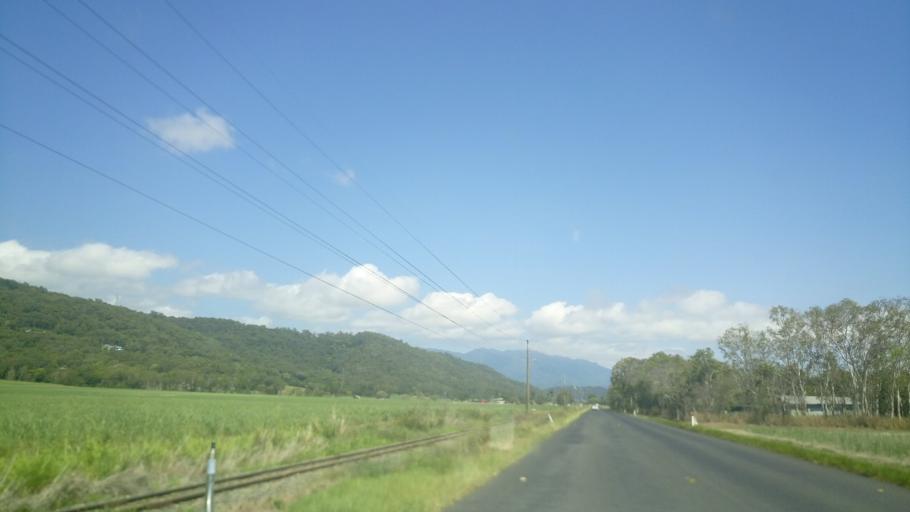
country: AU
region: Queensland
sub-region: Cairns
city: Port Douglas
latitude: -16.5003
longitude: 145.4333
